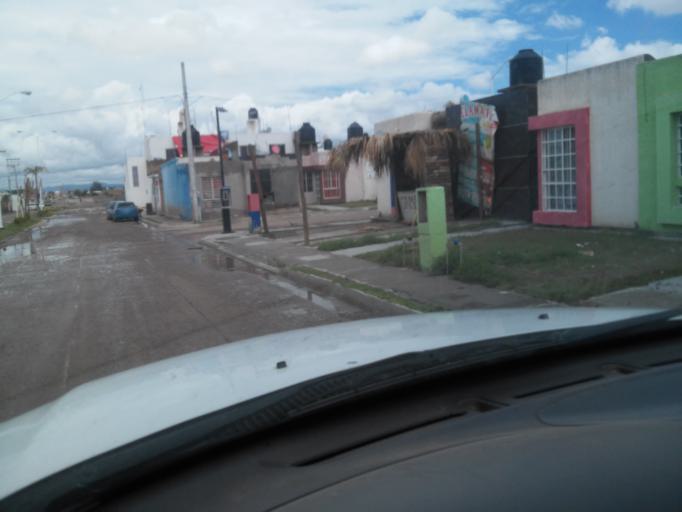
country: MX
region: Durango
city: Victoria de Durango
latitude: 24.0229
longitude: -104.6141
